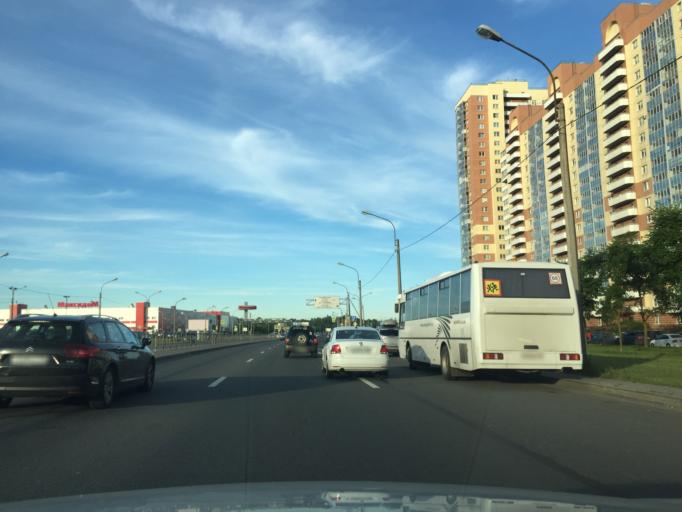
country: RU
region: St.-Petersburg
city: Obukhovo
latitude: 59.8440
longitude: 30.4170
